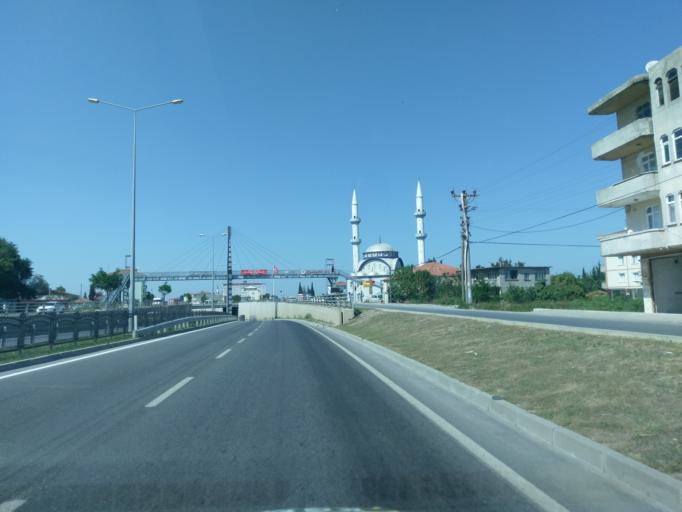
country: TR
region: Samsun
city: Bafra
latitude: 41.5501
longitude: 35.9263
